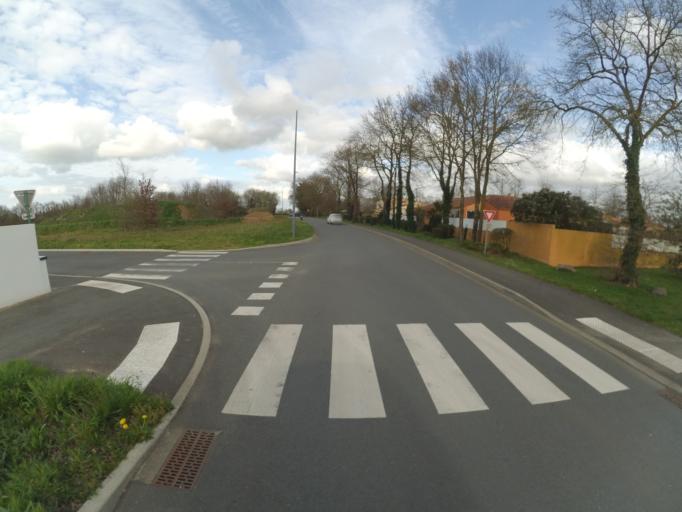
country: FR
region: Pays de la Loire
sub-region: Departement de la Vendee
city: Bouffere
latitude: 46.9664
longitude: -1.3400
